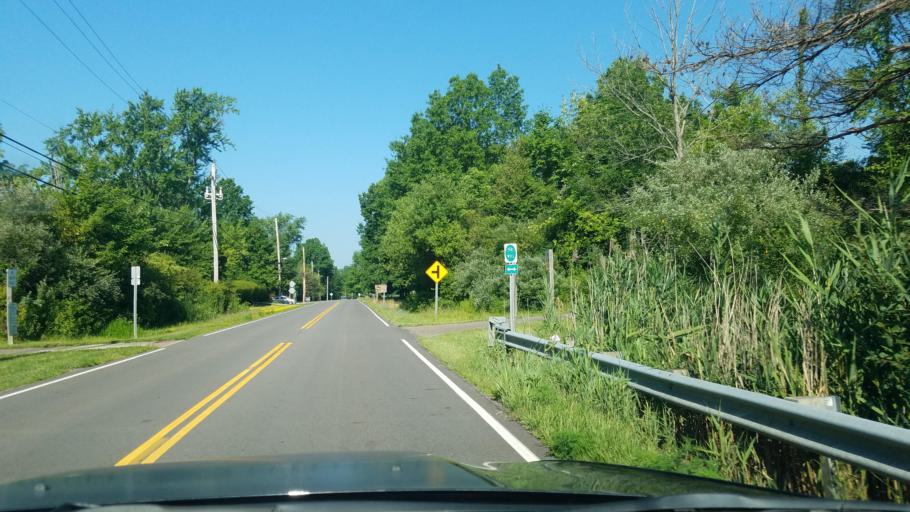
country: US
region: Ohio
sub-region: Trumbull County
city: Champion Heights
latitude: 41.2918
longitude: -80.8222
